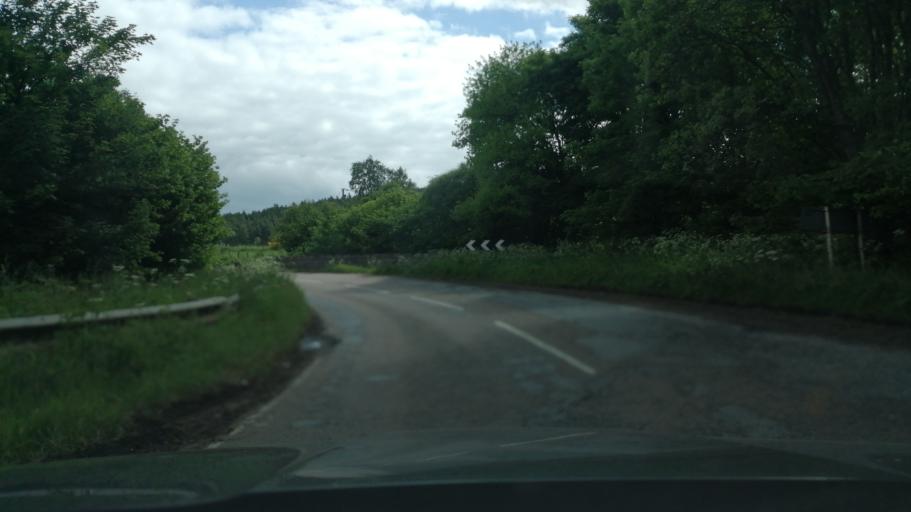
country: GB
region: Scotland
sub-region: Moray
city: Fochabers
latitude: 57.5465
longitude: -3.1185
